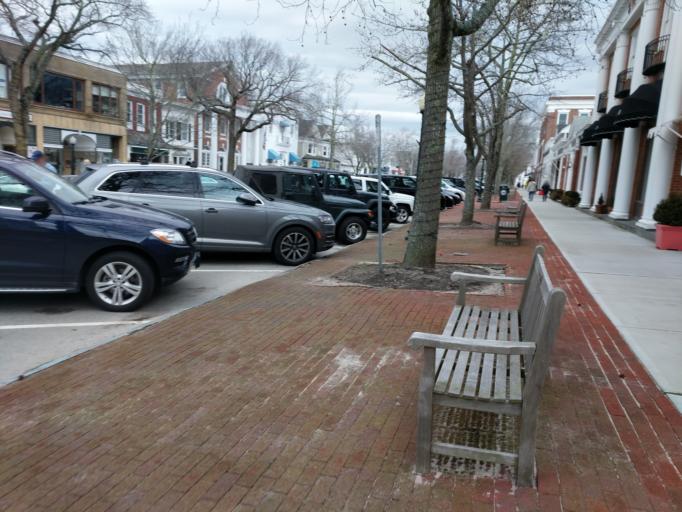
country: US
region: New York
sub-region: Suffolk County
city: Southampton
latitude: 40.8843
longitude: -72.3893
